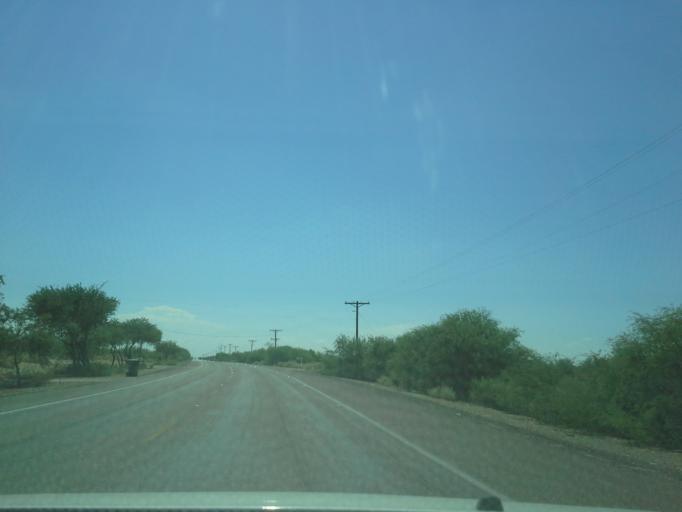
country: US
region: Arizona
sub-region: Maricopa County
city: Laveen
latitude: 33.2749
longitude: -112.1649
